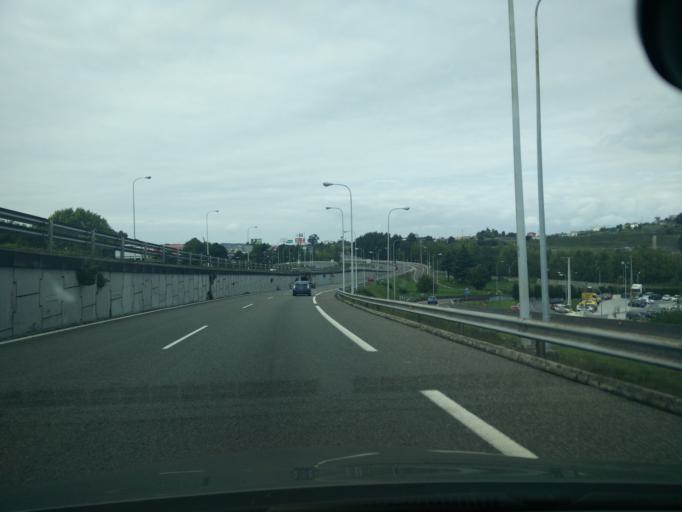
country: ES
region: Galicia
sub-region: Provincia da Coruna
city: Culleredo
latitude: 43.3275
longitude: -8.3959
